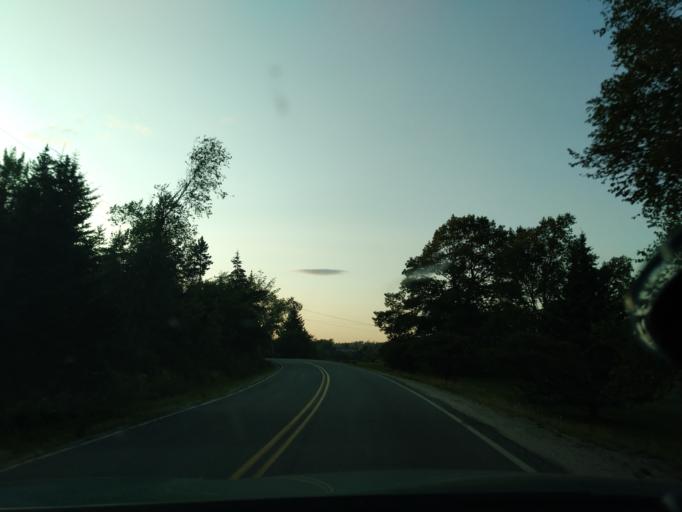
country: US
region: Maine
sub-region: Hancock County
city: Gouldsboro
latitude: 44.3834
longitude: -68.0364
